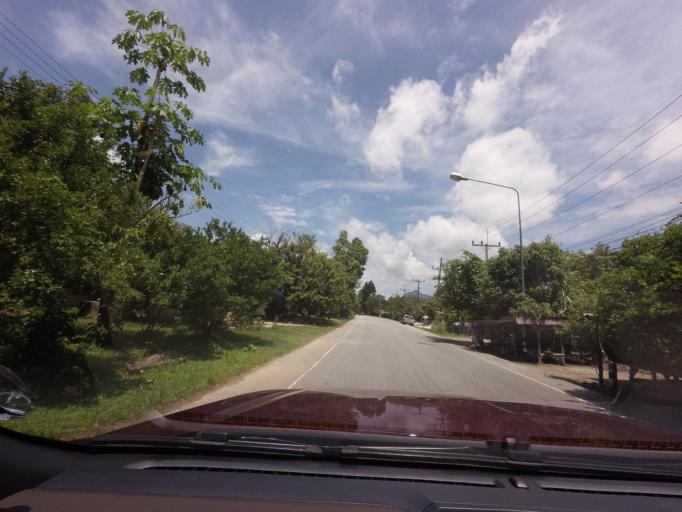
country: TH
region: Narathiwat
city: Ra-ngae
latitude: 6.2583
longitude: 101.6892
